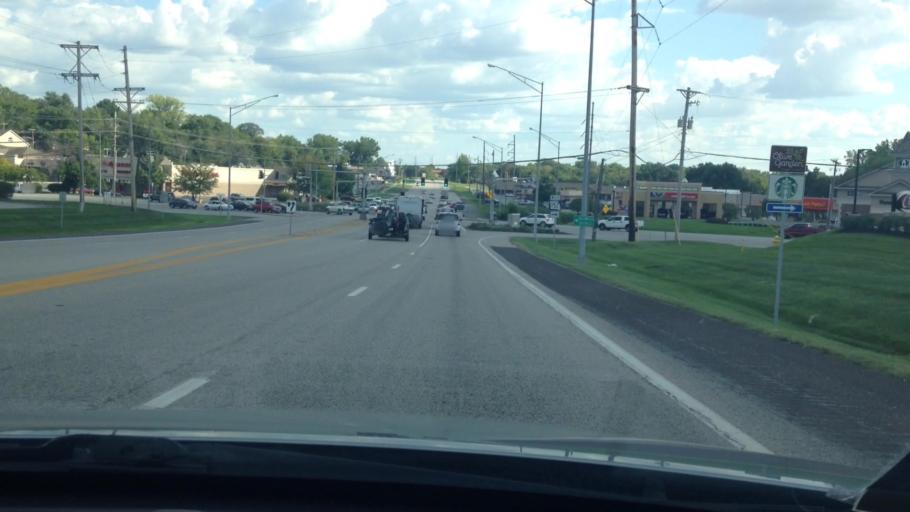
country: US
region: Missouri
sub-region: Clay County
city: Liberty
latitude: 39.2454
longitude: -94.4442
